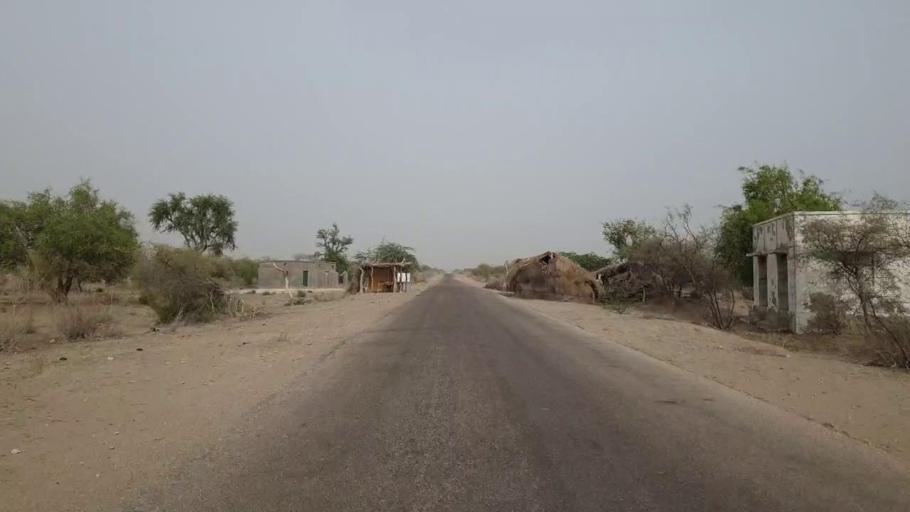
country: PK
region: Sindh
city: Islamkot
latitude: 24.5742
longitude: 70.3154
